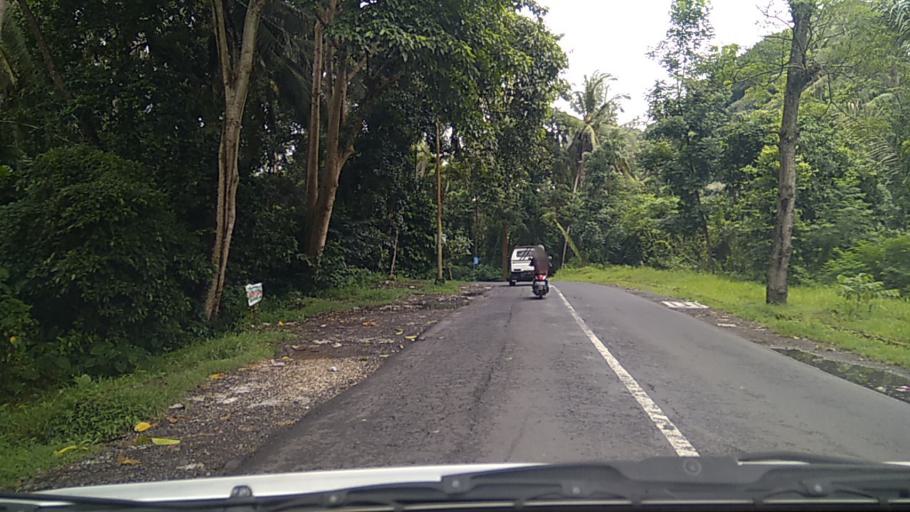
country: ID
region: Bali
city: Banjar Tebongkang
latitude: -8.5230
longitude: 115.2354
